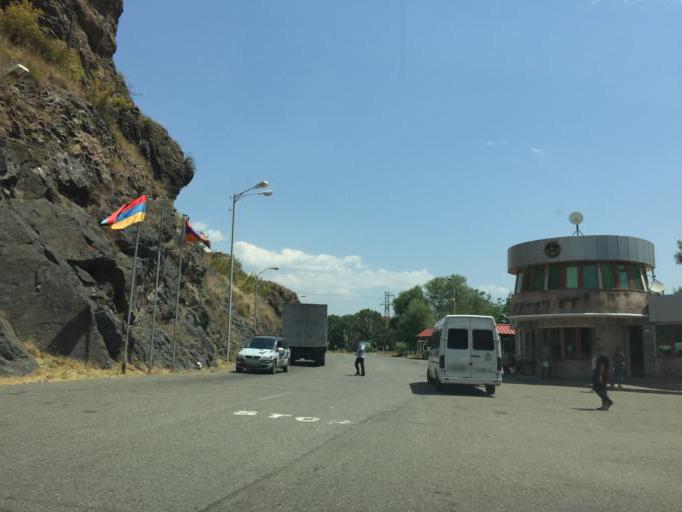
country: AZ
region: Lacin
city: Lacin
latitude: 39.5937
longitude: 46.5359
